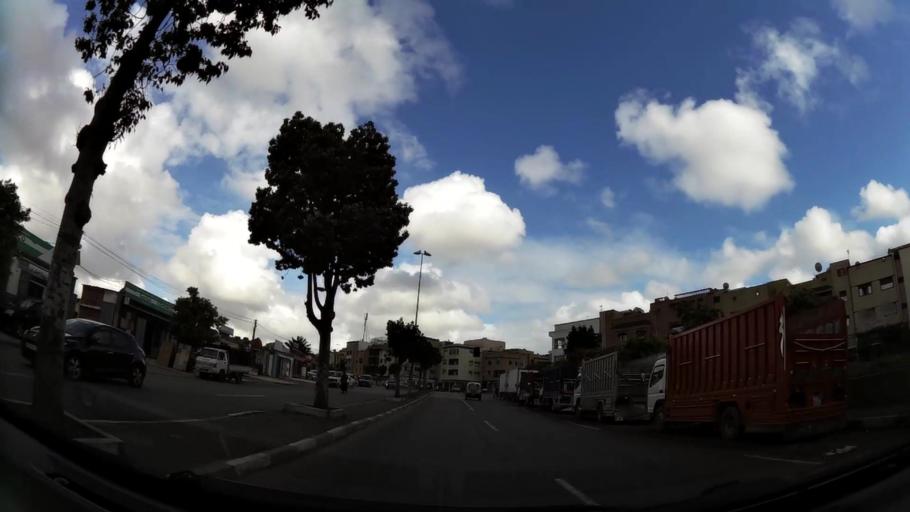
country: MA
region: Grand Casablanca
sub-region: Casablanca
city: Casablanca
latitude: 33.5469
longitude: -7.5963
